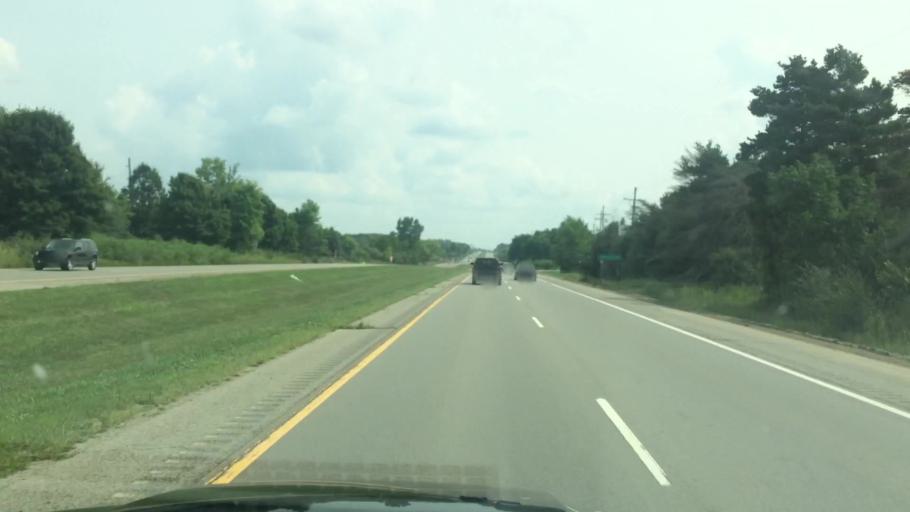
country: US
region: Michigan
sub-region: Oakland County
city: Oxford
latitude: 42.8628
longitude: -83.2911
